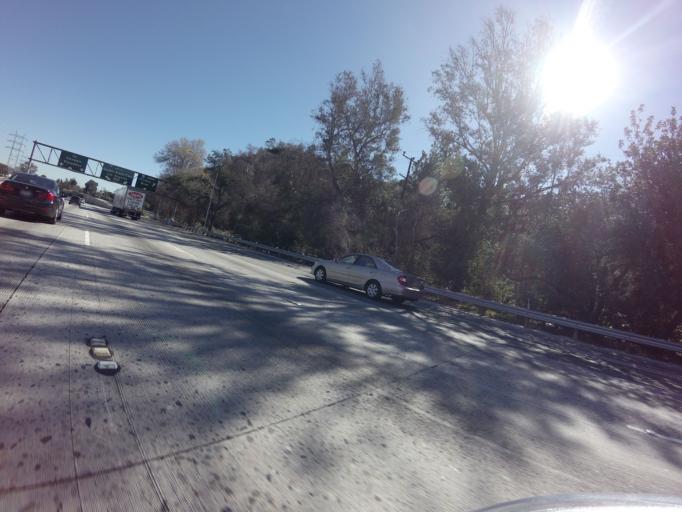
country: US
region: California
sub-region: Los Angeles County
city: Burbank
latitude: 34.1556
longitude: -118.2973
